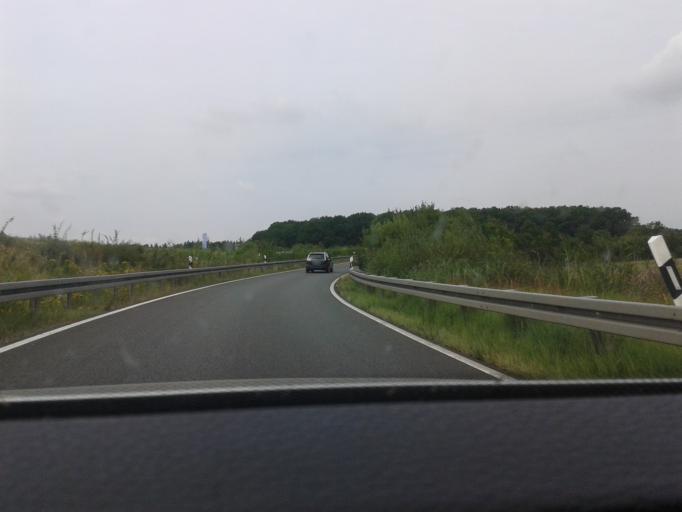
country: DE
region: Lower Saxony
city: Lehre
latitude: 52.3094
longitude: 10.7307
